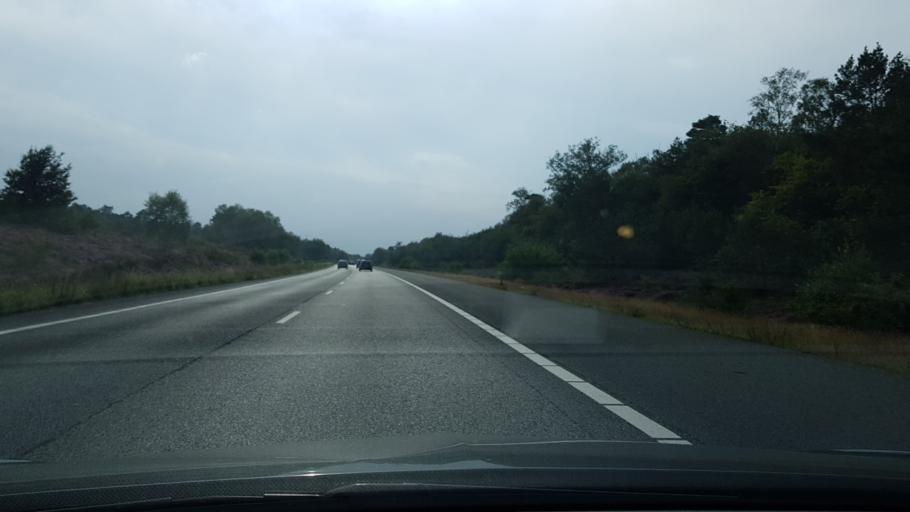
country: NL
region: Gelderland
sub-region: Gemeente Apeldoorn
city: Uddel
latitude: 52.2033
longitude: 5.8035
